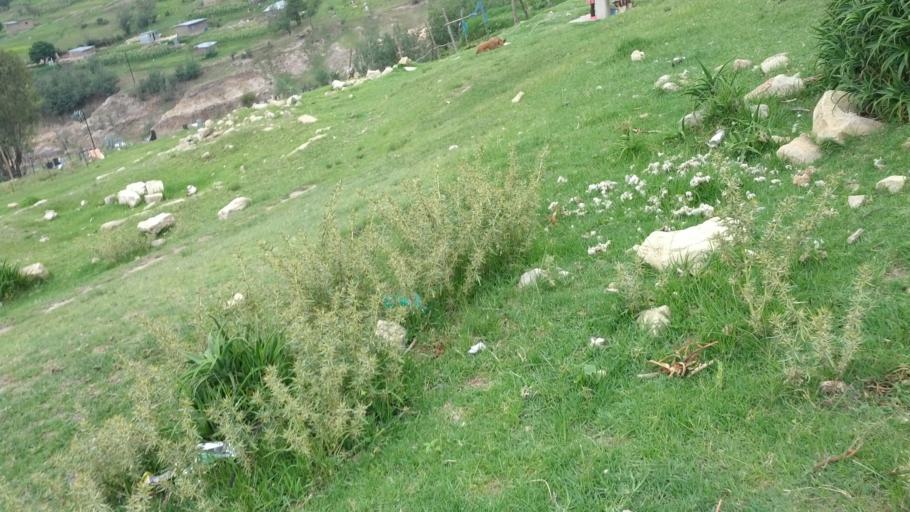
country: LS
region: Leribe
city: Leribe
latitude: -29.0352
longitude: 28.0216
